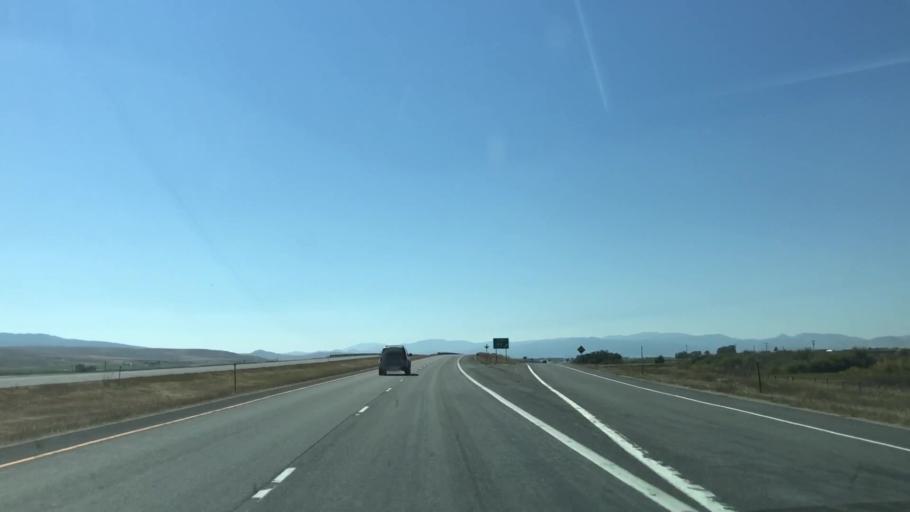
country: US
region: Montana
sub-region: Deer Lodge County
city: Warm Springs
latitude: 46.2411
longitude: -112.7640
